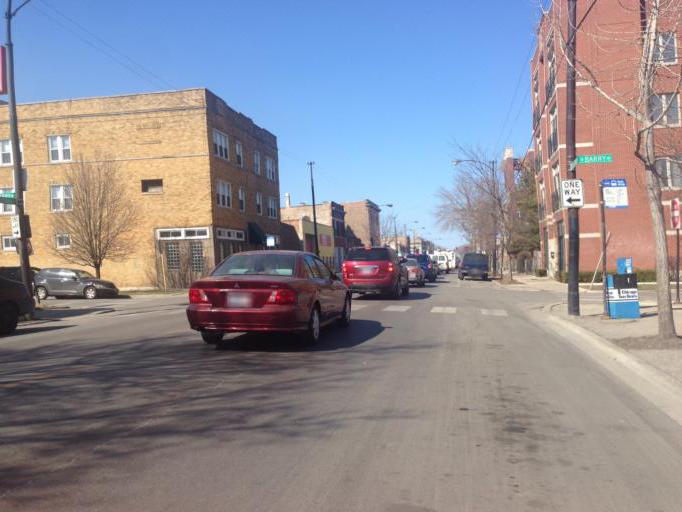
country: US
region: Illinois
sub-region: Cook County
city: Lincolnwood
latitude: 41.9373
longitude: -87.6977
